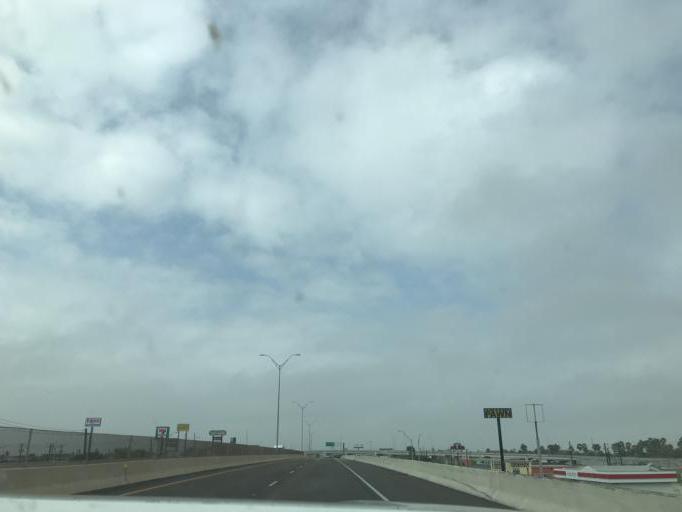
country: US
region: Texas
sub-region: Nueces County
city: Corpus Christi
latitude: 27.6678
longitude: -97.2811
